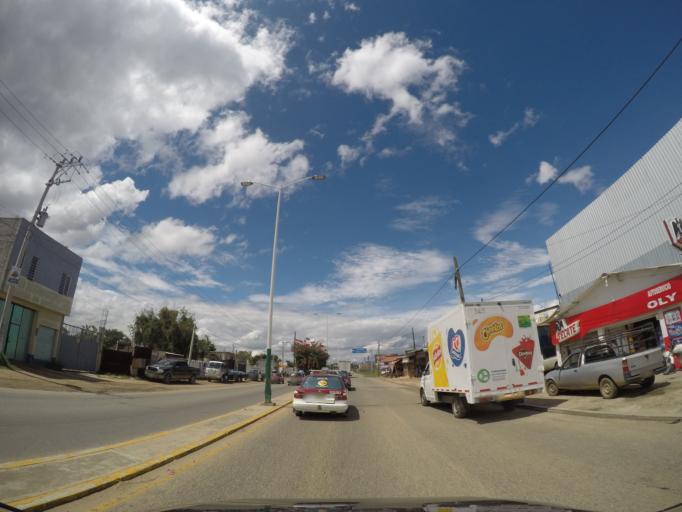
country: MX
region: Oaxaca
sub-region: Santa Cruz Xoxocotlan
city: Santa Cruz Xoxocotlan
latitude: 17.0191
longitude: -96.7318
